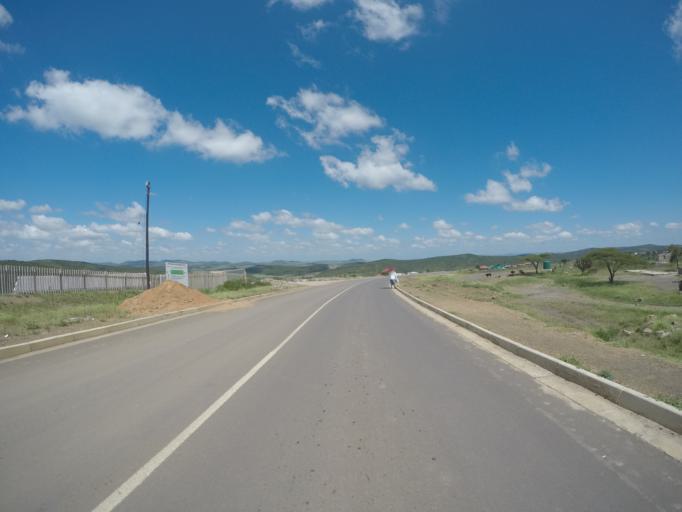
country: ZA
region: KwaZulu-Natal
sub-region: uThungulu District Municipality
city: Empangeni
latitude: -28.6068
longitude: 31.7464
